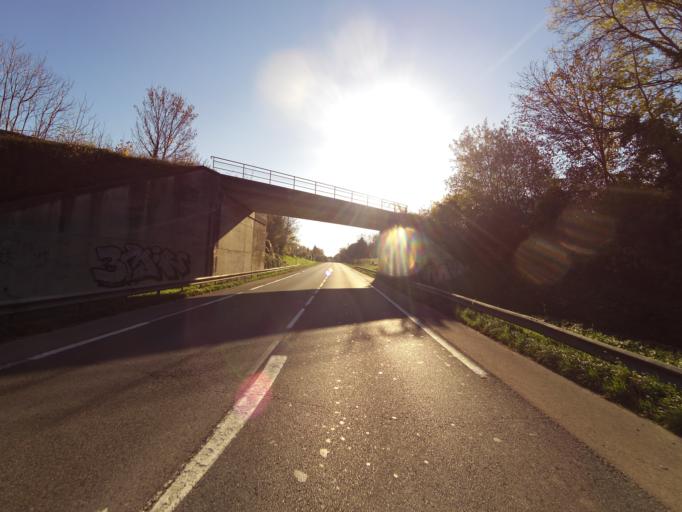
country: FR
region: Champagne-Ardenne
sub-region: Departement de l'Aube
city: Breviandes
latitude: 48.2583
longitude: 4.0986
